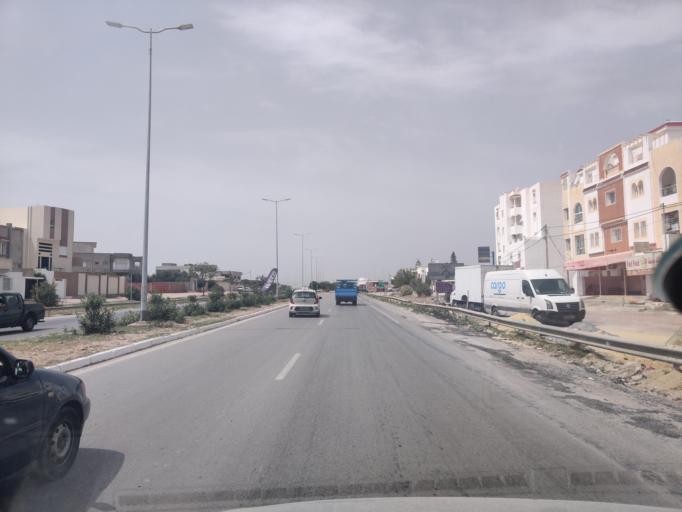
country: TN
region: Susah
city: Akouda
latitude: 35.8348
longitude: 10.5614
